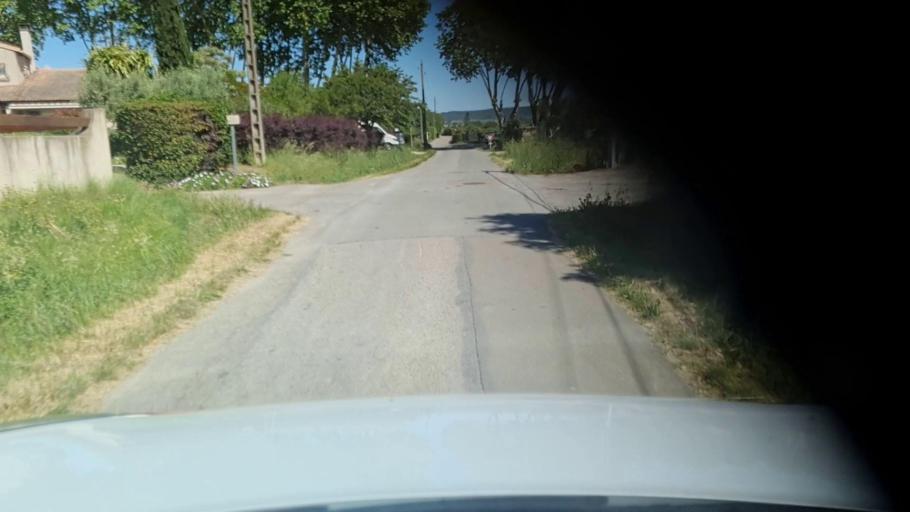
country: FR
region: Languedoc-Roussillon
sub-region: Departement du Gard
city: Clarensac
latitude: 43.8253
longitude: 4.2014
